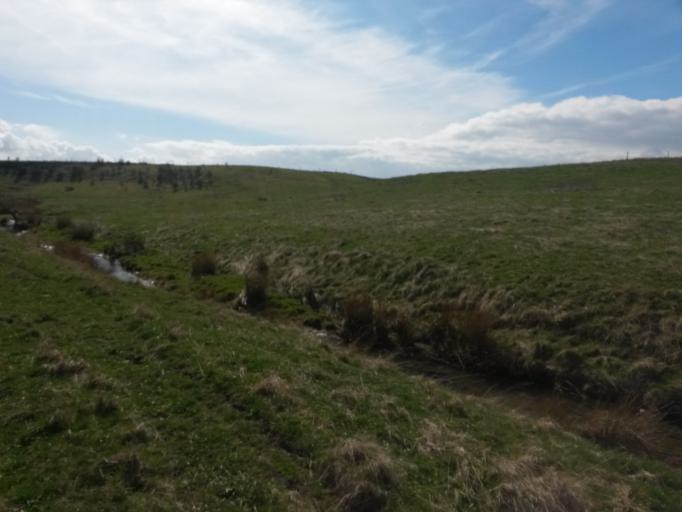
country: SE
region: Skane
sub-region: Kavlinge Kommun
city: Kaevlinge
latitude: 55.7792
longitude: 13.1622
